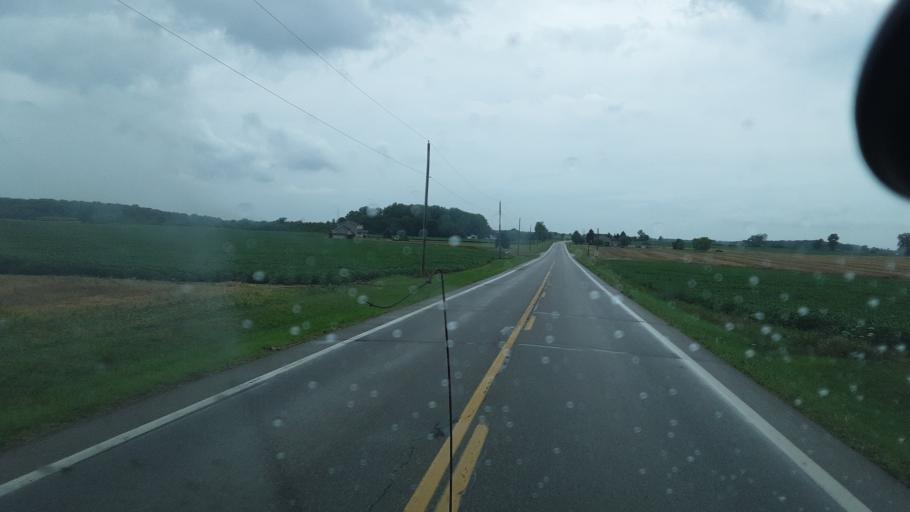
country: US
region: Ohio
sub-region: Williams County
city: Edgerton
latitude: 41.5564
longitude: -84.7962
